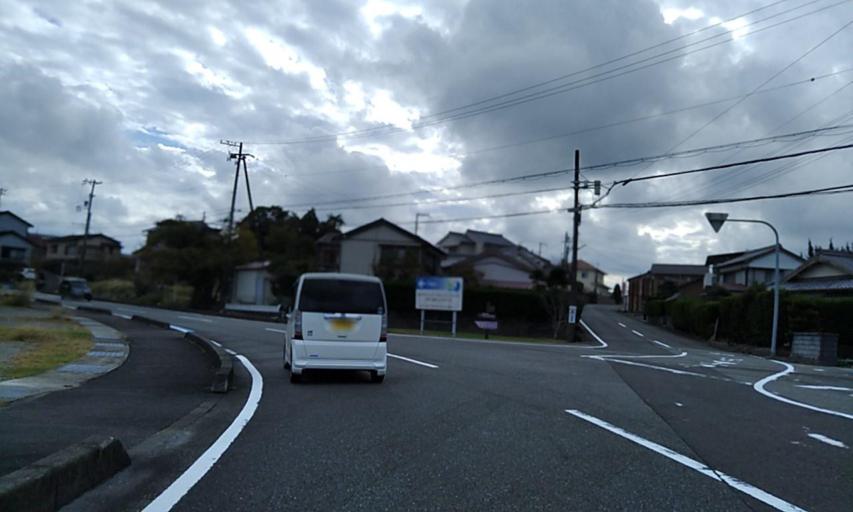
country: JP
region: Wakayama
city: Shingu
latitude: 33.5865
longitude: 135.9478
